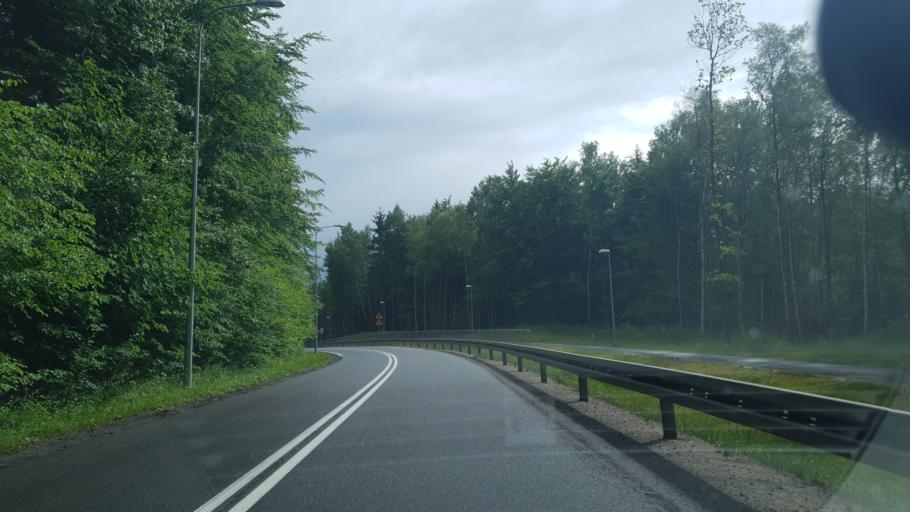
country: PL
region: Pomeranian Voivodeship
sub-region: Powiat kartuski
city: Kartuzy
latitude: 54.3475
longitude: 18.2150
